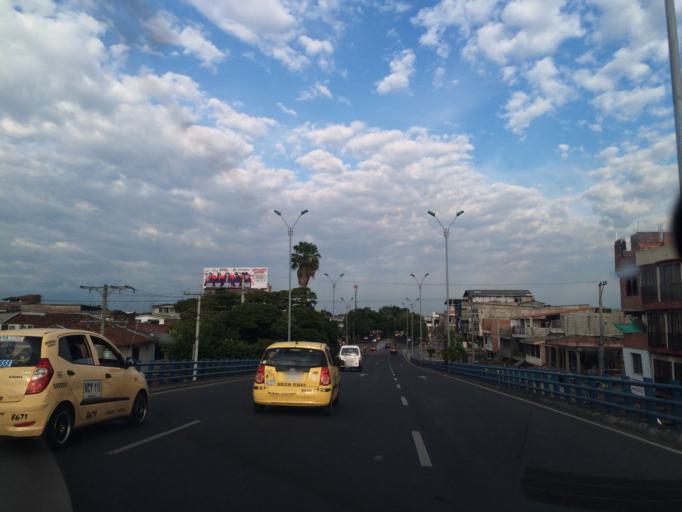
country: CO
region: Valle del Cauca
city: Cali
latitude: 3.4156
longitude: -76.5363
